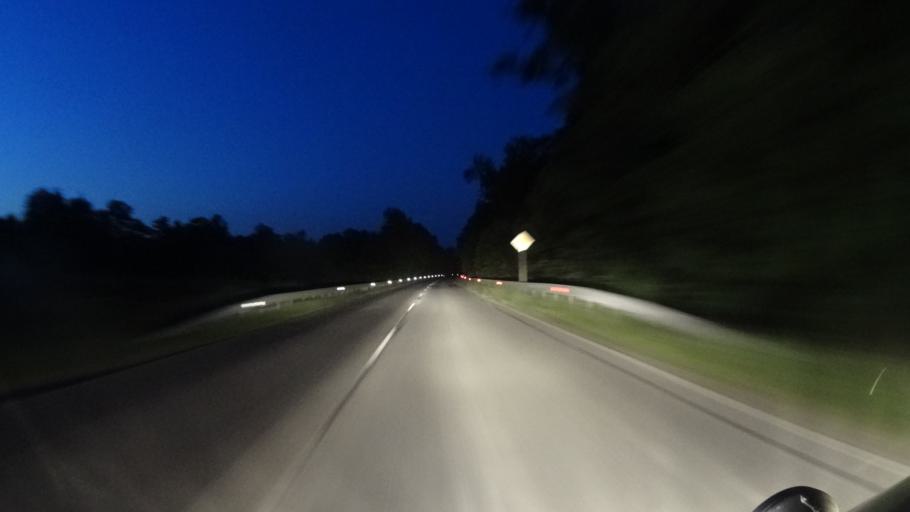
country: HU
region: Somogy
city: Balatonbereny
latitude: 46.6847
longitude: 17.3454
